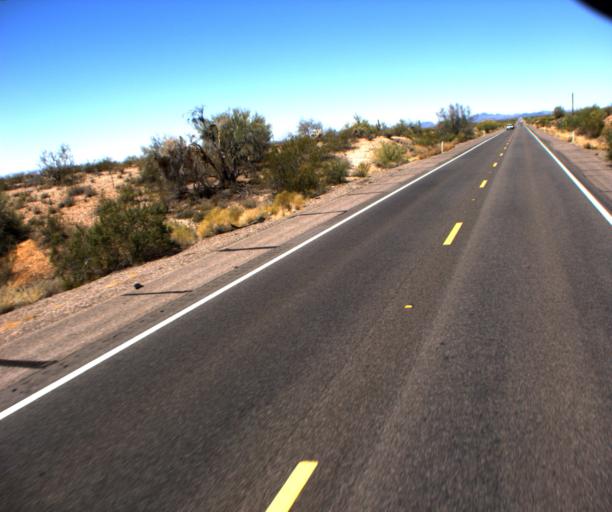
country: US
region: Arizona
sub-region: Maricopa County
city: Sun City West
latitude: 33.8391
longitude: -112.4852
